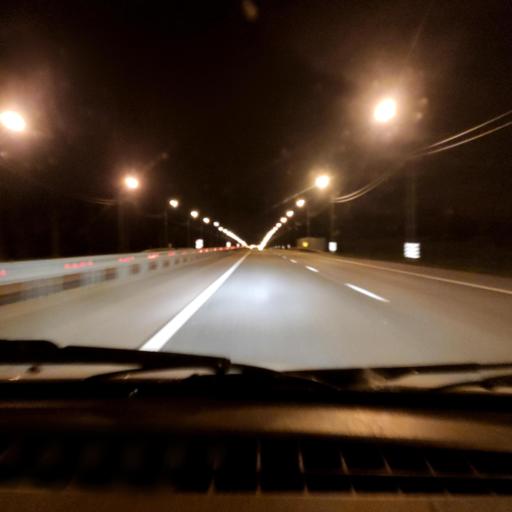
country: RU
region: Lipetsk
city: Zadonsk
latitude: 52.3319
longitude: 39.0059
